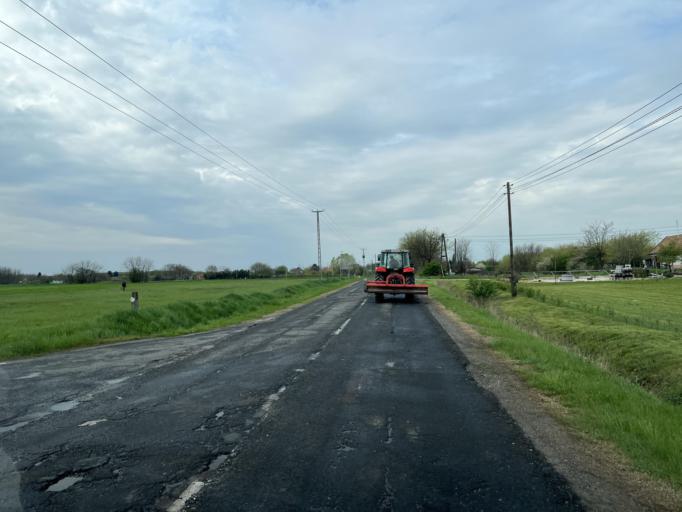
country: HU
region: Pest
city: Albertirsa
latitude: 47.2411
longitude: 19.5954
